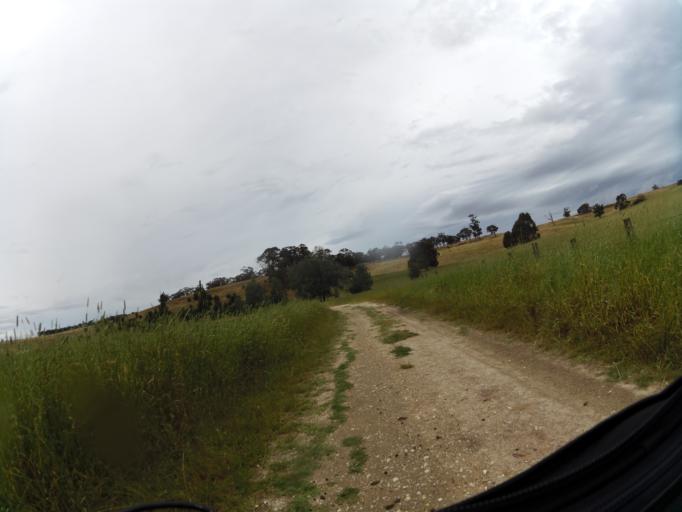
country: AU
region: Victoria
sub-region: Mount Alexander
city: Castlemaine
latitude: -37.2097
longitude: 144.0265
